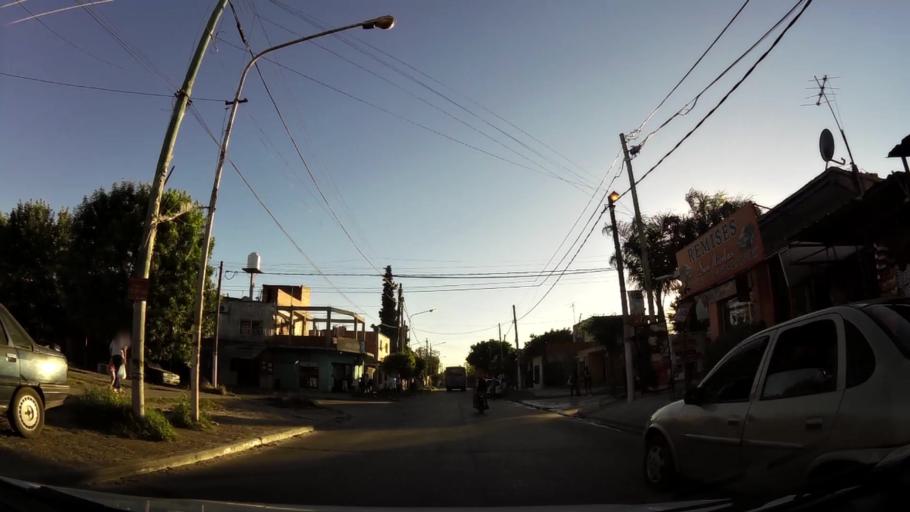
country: AR
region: Buenos Aires
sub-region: Partido de Moron
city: Moron
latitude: -34.7147
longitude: -58.6140
